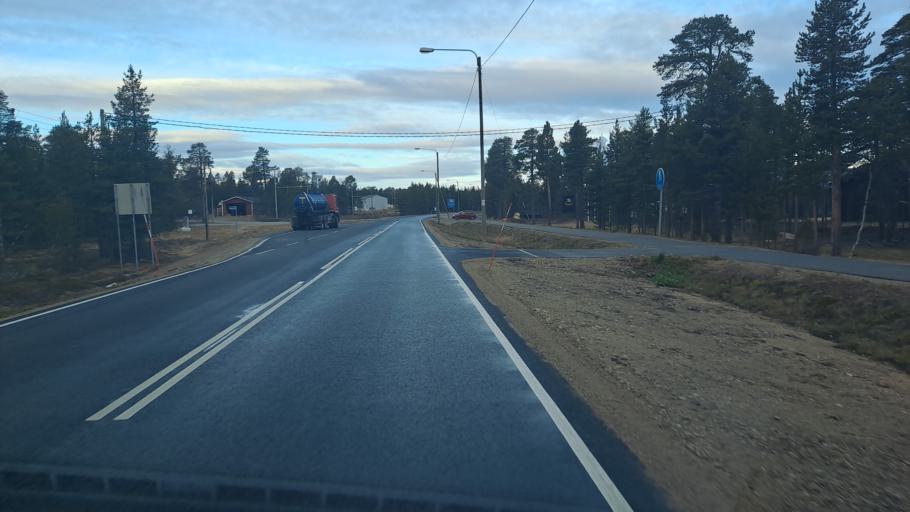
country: FI
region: Lapland
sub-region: Pohjois-Lappi
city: Inari
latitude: 68.8975
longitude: 27.0875
